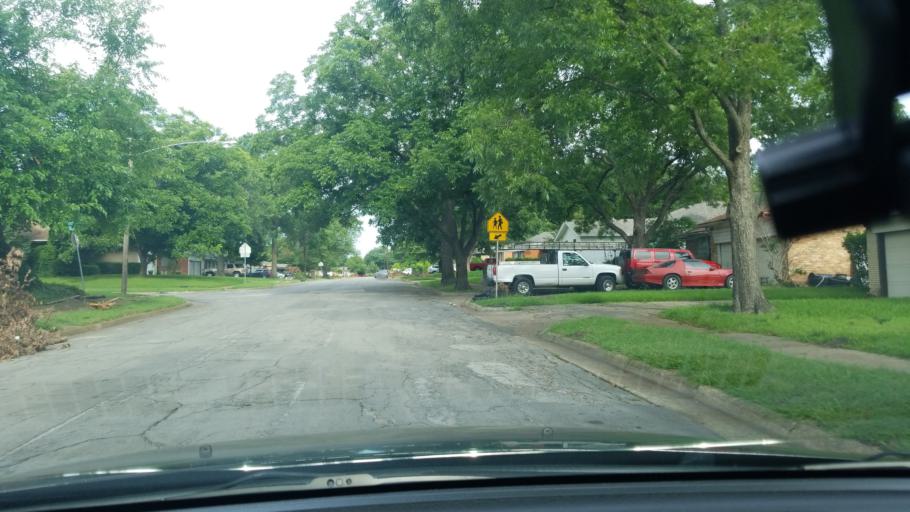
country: US
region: Texas
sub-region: Dallas County
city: Balch Springs
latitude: 32.7544
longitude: -96.6699
